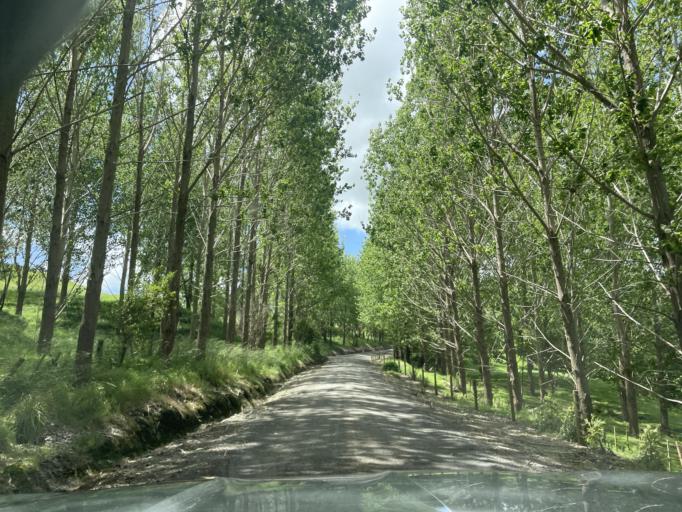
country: NZ
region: Auckland
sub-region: Auckland
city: Wellsford
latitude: -36.1757
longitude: 174.3154
